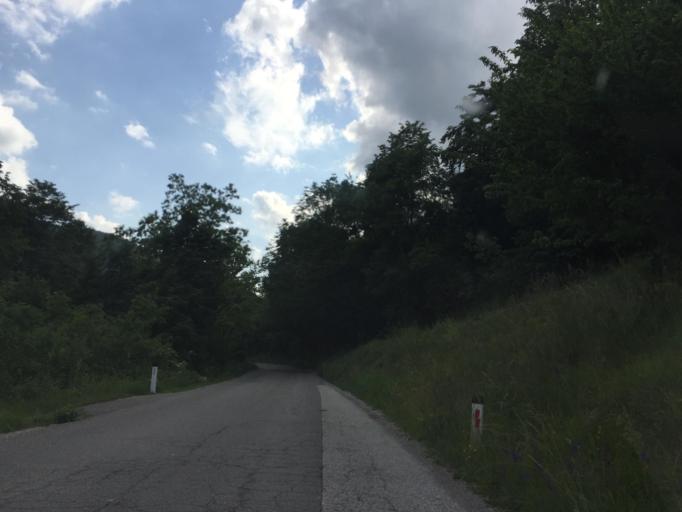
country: SI
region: Nova Gorica
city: Sempas
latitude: 46.0168
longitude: 13.7409
